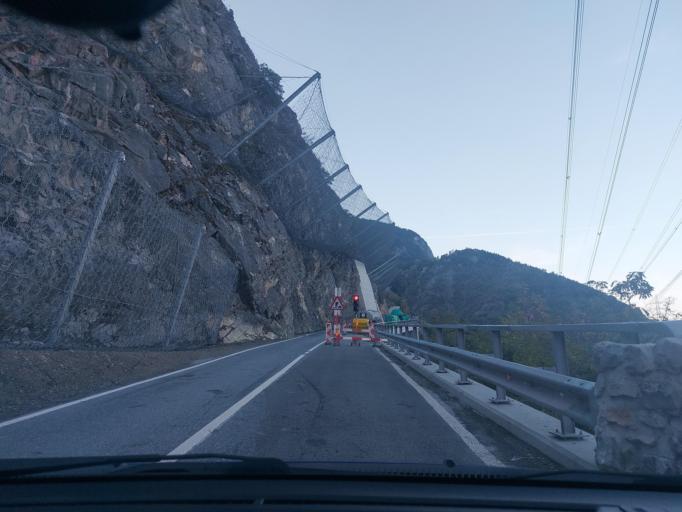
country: CH
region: Valais
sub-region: Sierre District
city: Chippis
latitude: 46.2810
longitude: 7.5507
